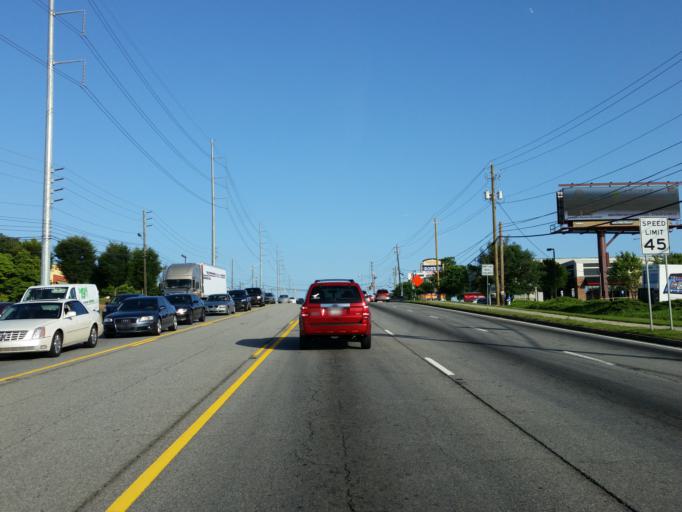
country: US
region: Georgia
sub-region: Cobb County
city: Vinings
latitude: 33.8918
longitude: -84.4772
